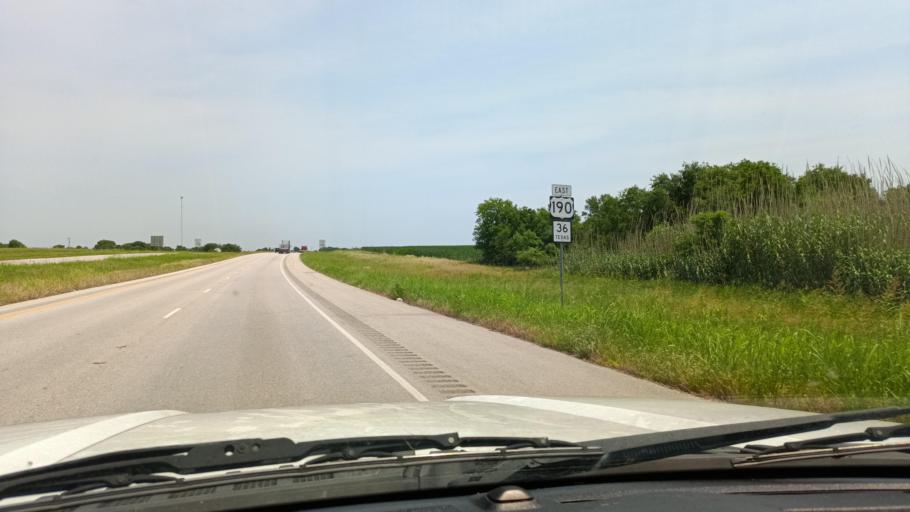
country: US
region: Texas
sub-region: Bell County
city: Little River-Academy
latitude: 31.0090
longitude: -97.2967
